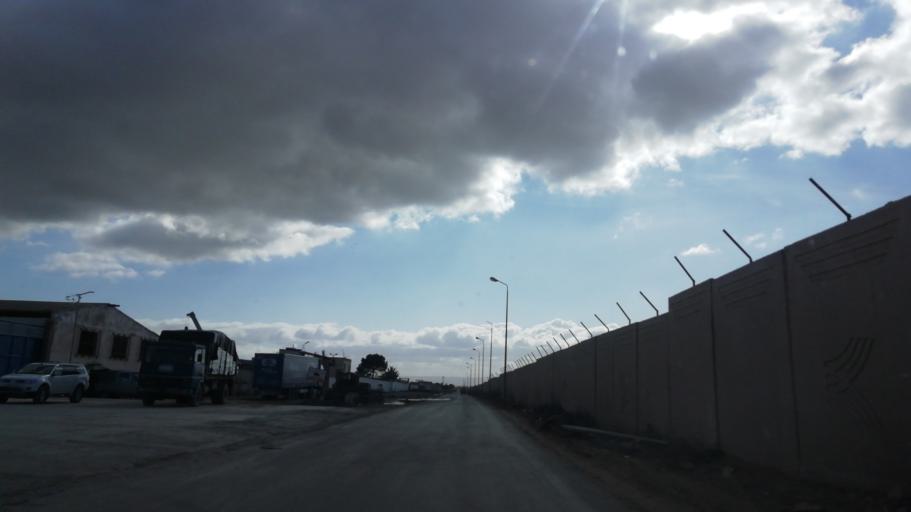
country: DZ
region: Oran
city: Es Senia
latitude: 35.6367
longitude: -0.5981
